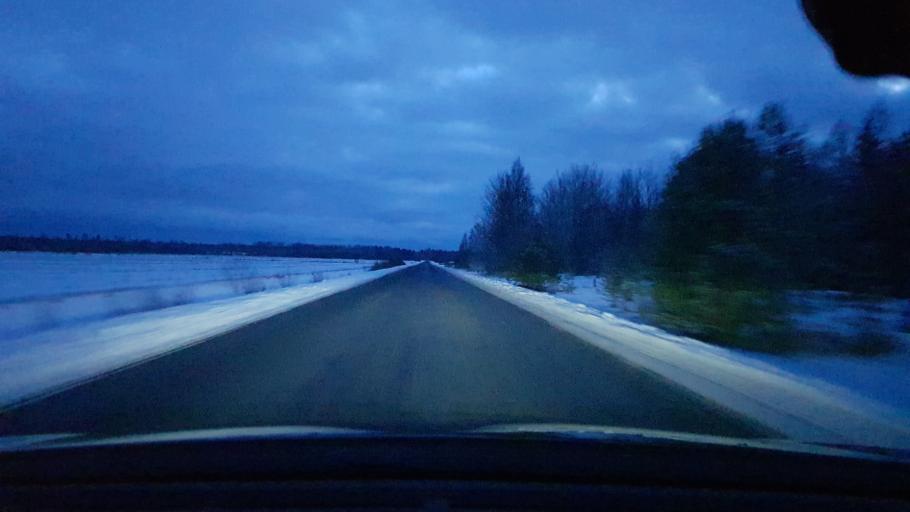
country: EE
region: Harju
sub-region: Nissi vald
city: Riisipere
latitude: 59.2182
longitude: 24.2486
